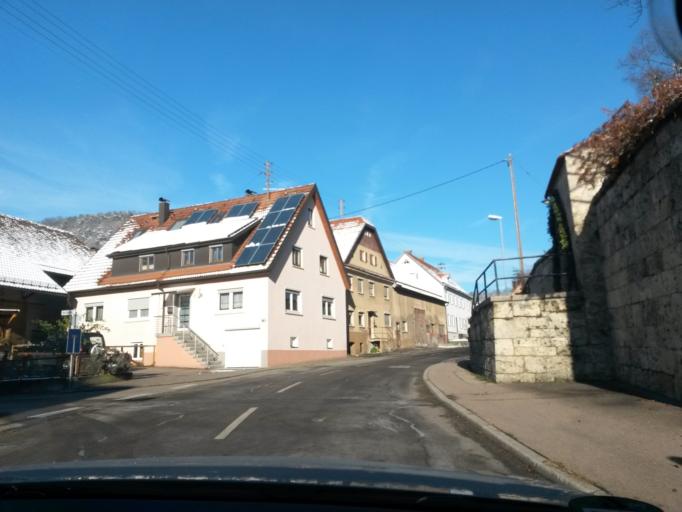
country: DE
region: Baden-Wuerttemberg
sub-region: Regierungsbezirk Stuttgart
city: Gingen an der Fils
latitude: 48.6275
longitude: 9.7610
